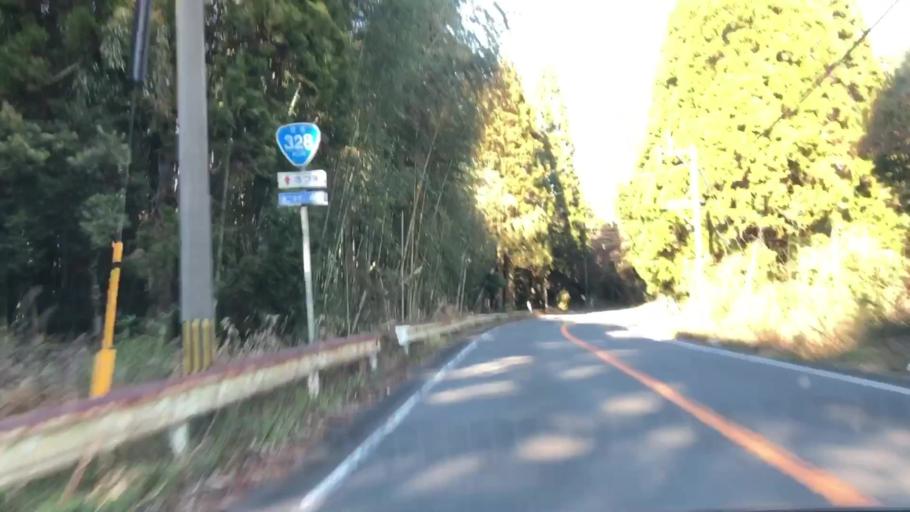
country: JP
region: Kagoshima
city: Satsumasendai
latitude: 31.8561
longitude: 130.4294
